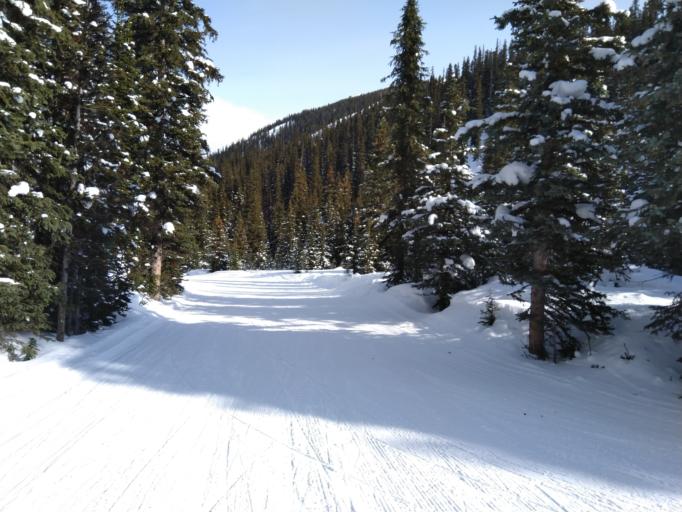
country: CA
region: Alberta
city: Banff
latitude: 51.0884
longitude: -115.7676
